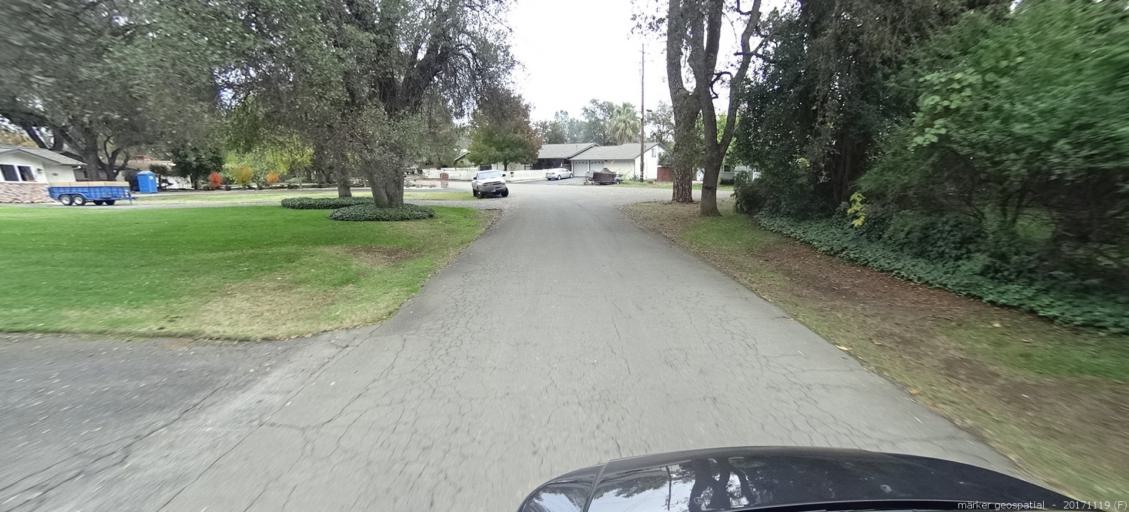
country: US
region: California
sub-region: Shasta County
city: Anderson
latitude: 40.4933
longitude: -122.3463
